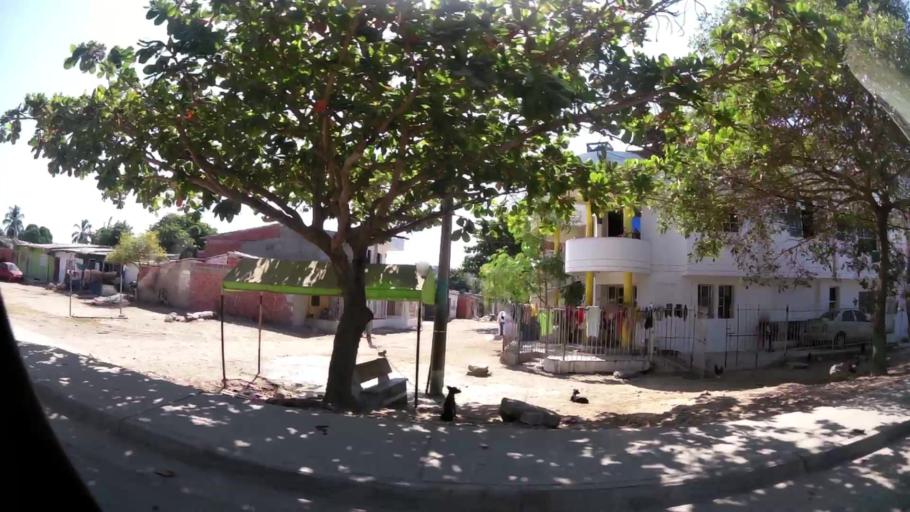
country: CO
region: Bolivar
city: Cartagena
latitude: 10.4378
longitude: -75.5289
